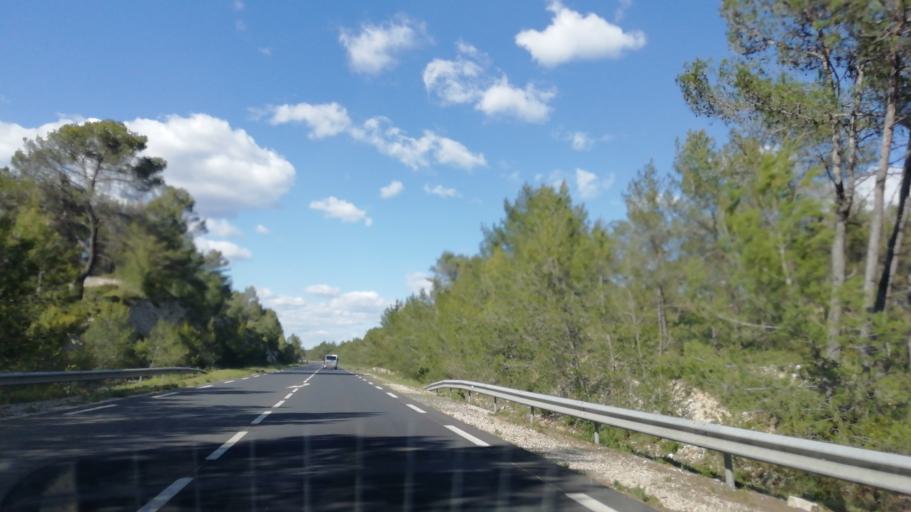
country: FR
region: Languedoc-Roussillon
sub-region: Departement de l'Herault
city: Saint-Clement-de-Riviere
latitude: 43.6897
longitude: 3.8242
